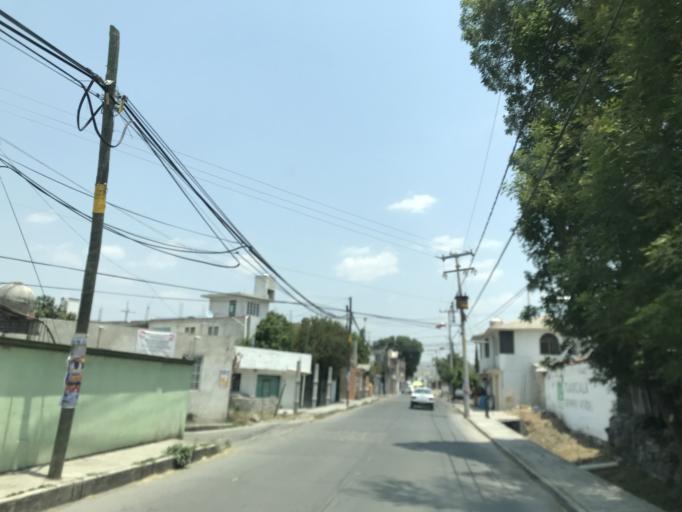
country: MX
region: Tlaxcala
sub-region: Ixtacuixtla de Mariano Matamoros
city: Villa Mariano Matamoros
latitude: 19.3105
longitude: -98.3722
